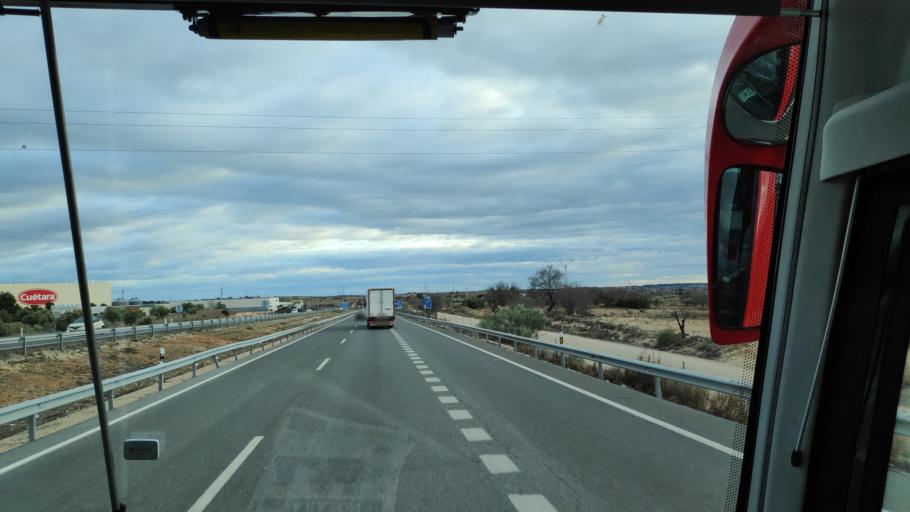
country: ES
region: Madrid
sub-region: Provincia de Madrid
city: Villarejo de Salvanes
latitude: 40.1805
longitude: -3.2969
